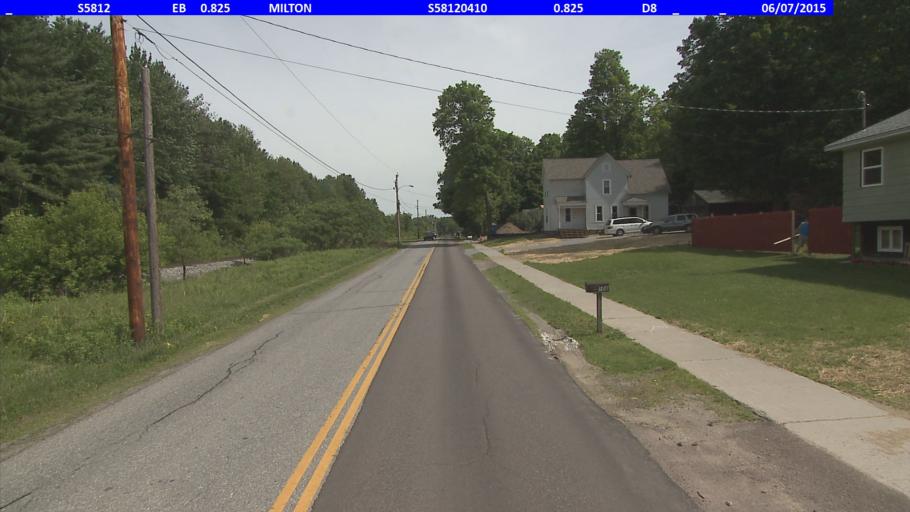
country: US
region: Vermont
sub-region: Chittenden County
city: Milton
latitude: 44.6305
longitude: -73.1073
